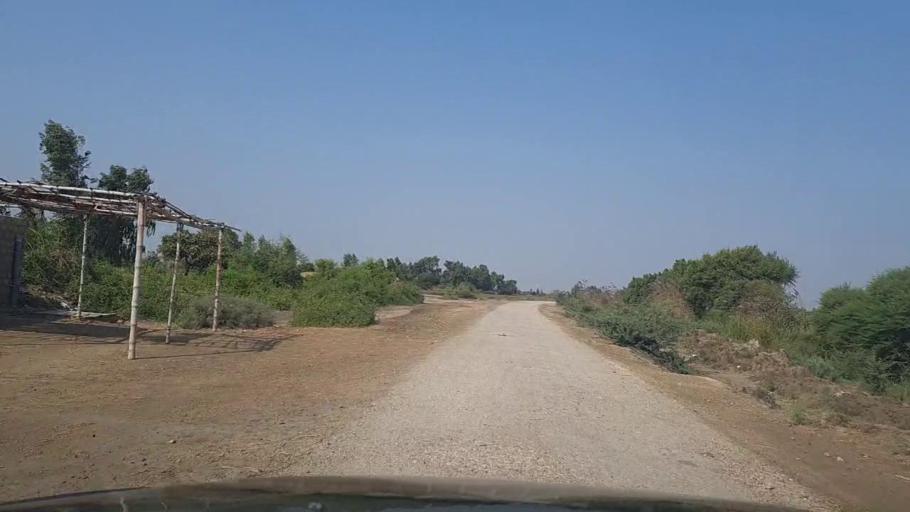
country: PK
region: Sindh
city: Thatta
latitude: 24.6177
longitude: 67.8176
